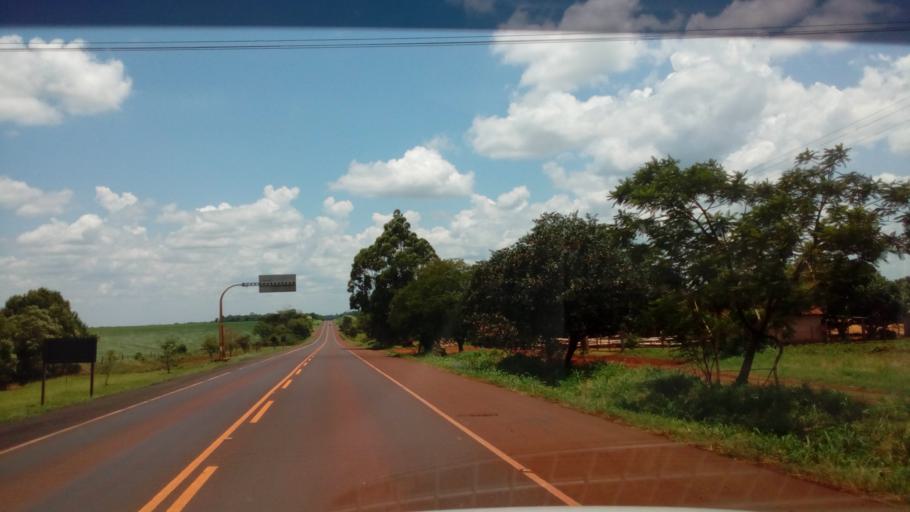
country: PY
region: Itapua
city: Edelira
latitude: -26.7657
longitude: -55.3865
